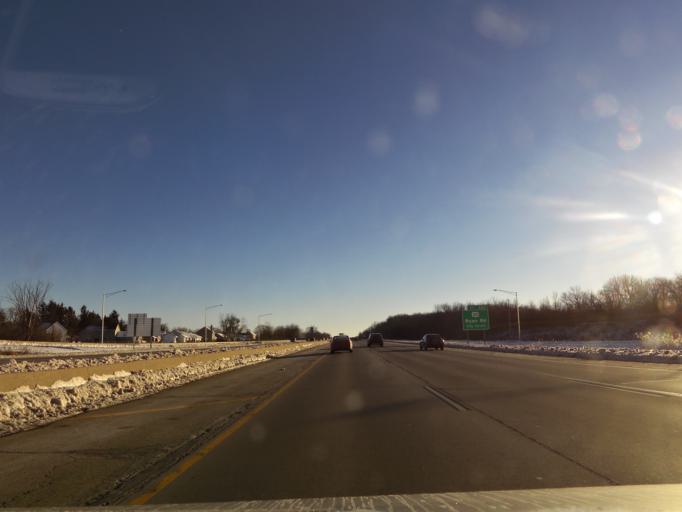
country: US
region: Wisconsin
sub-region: Milwaukee County
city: Greendale
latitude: 42.9002
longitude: -87.9364
